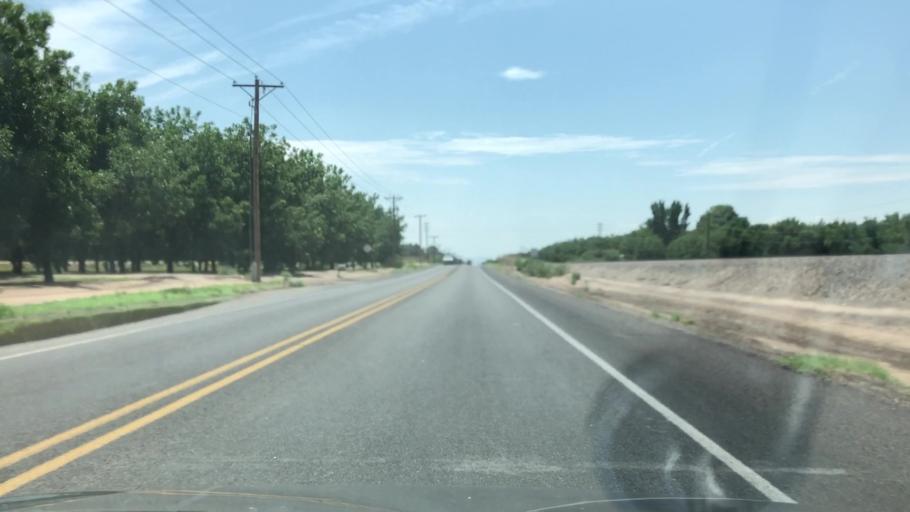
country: US
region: New Mexico
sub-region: Dona Ana County
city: University Park
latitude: 32.2283
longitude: -106.7369
